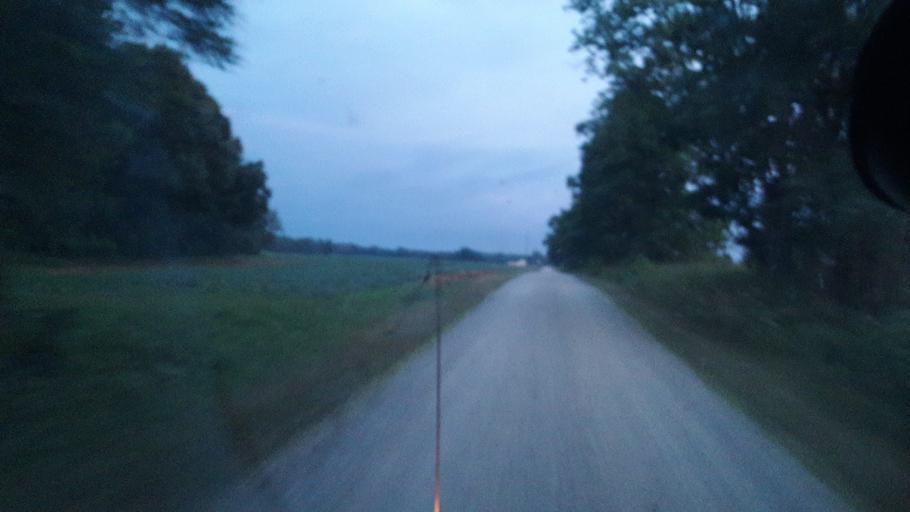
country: US
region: Ohio
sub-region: Defiance County
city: Hicksville
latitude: 41.3680
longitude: -84.8054
